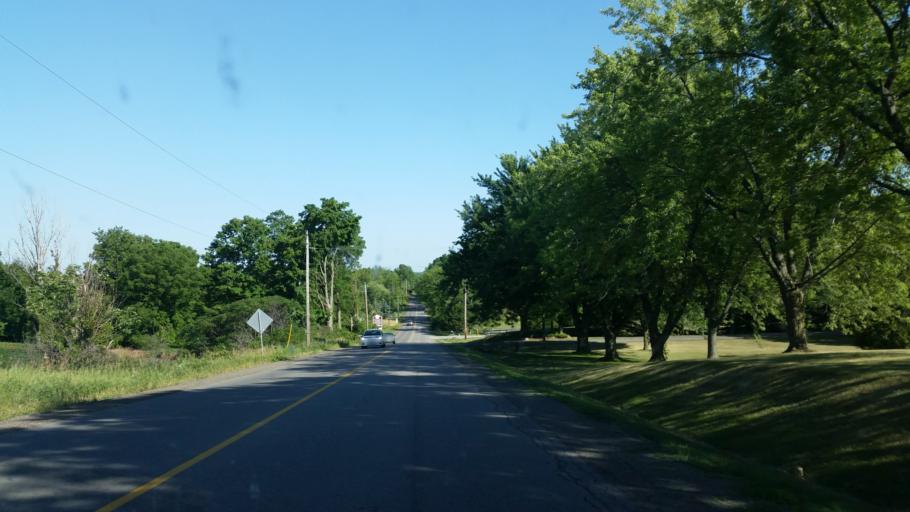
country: CA
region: Ontario
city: Bradford West Gwillimbury
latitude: 43.9555
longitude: -79.7710
